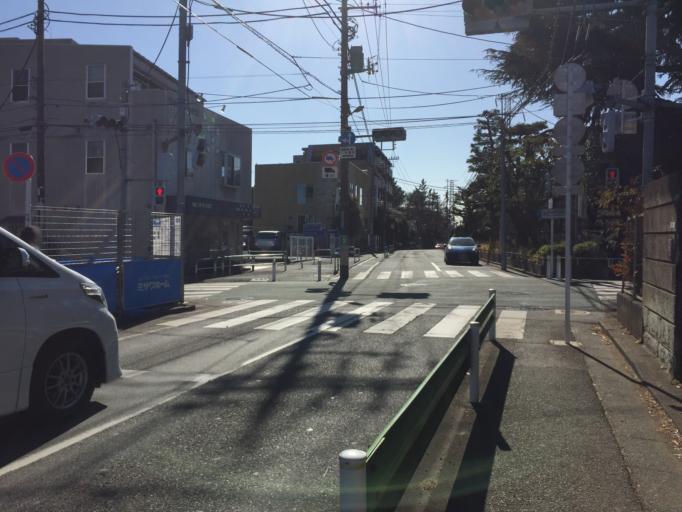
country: JP
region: Tokyo
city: Chofugaoka
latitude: 35.6357
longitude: 139.5999
